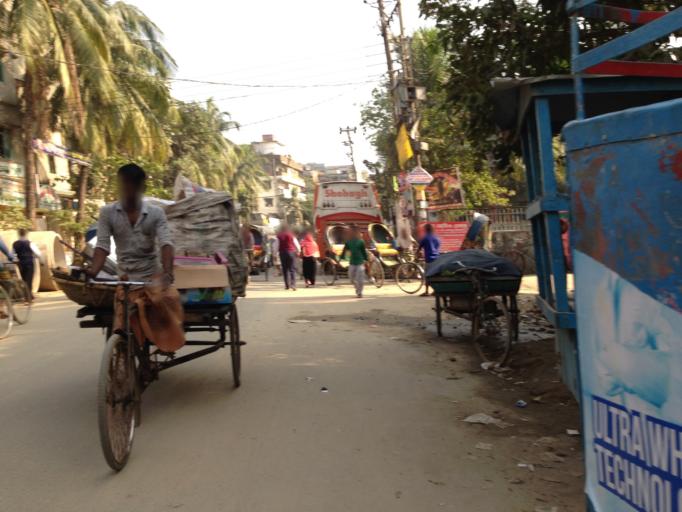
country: BD
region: Dhaka
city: Azimpur
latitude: 23.8023
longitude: 90.3489
